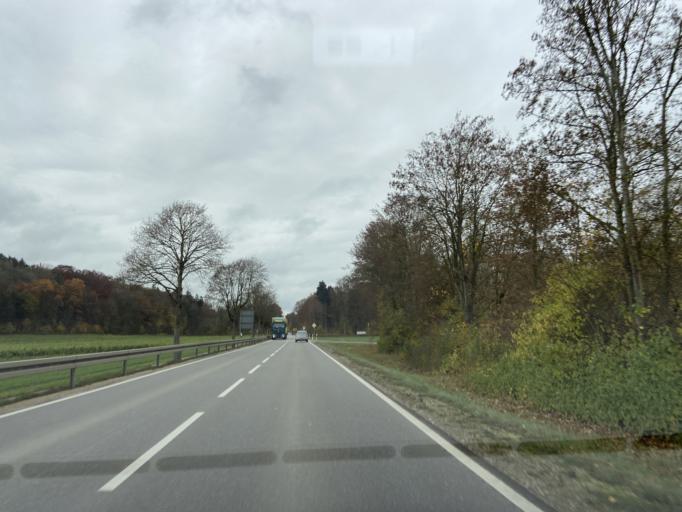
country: DE
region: Baden-Wuerttemberg
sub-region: Tuebingen Region
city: Krauchenwies
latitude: 48.0274
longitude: 9.2491
